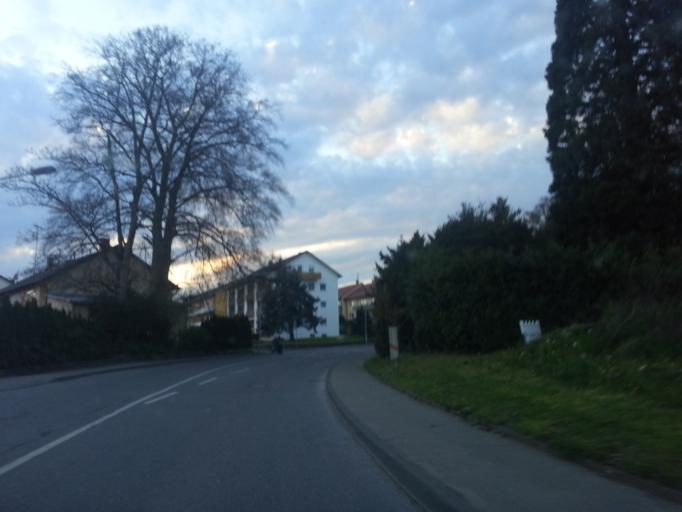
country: DE
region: Bavaria
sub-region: Swabia
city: Lindau
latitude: 47.5526
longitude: 9.6927
